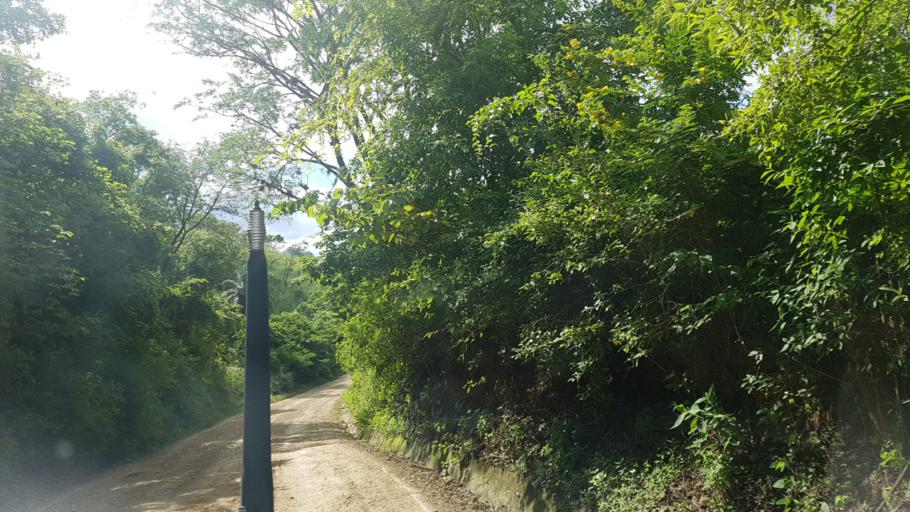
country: HN
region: El Paraiso
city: Oropoli
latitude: 13.7442
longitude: -86.7067
